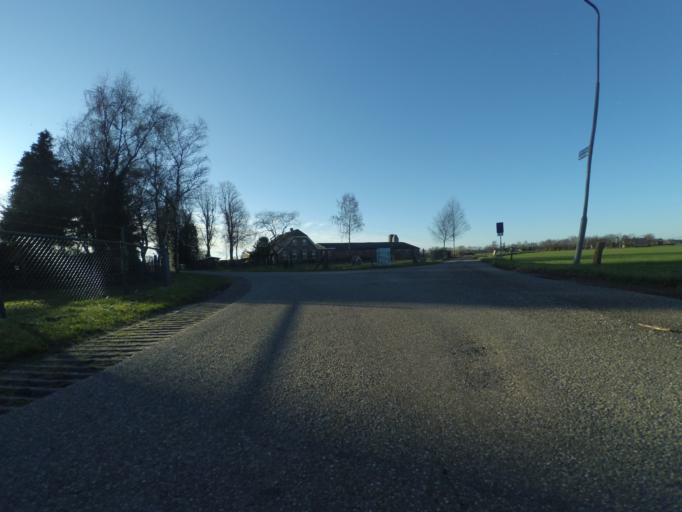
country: NL
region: Gelderland
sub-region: Gemeente Putten
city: Putten
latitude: 52.2486
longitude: 5.5752
